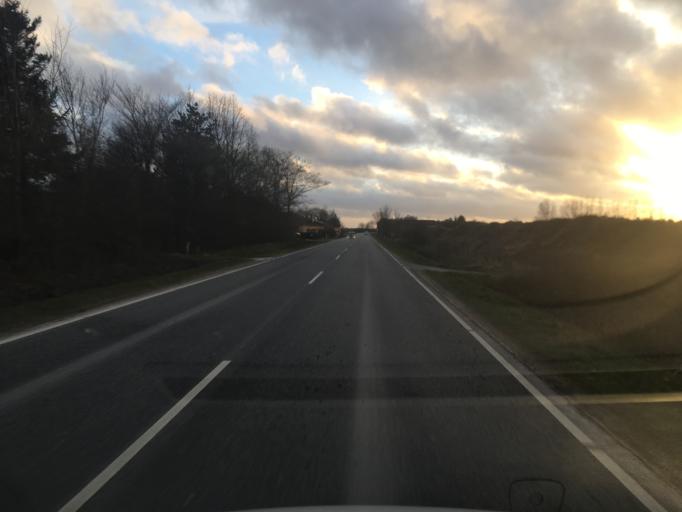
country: DK
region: South Denmark
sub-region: Aabenraa Kommune
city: Tinglev
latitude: 54.9681
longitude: 9.3067
